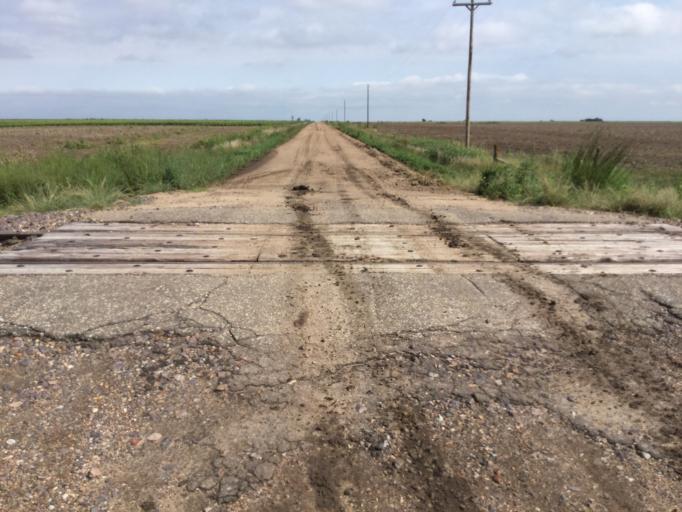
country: US
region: Kansas
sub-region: Rush County
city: La Crosse
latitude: 38.5433
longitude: -99.3468
